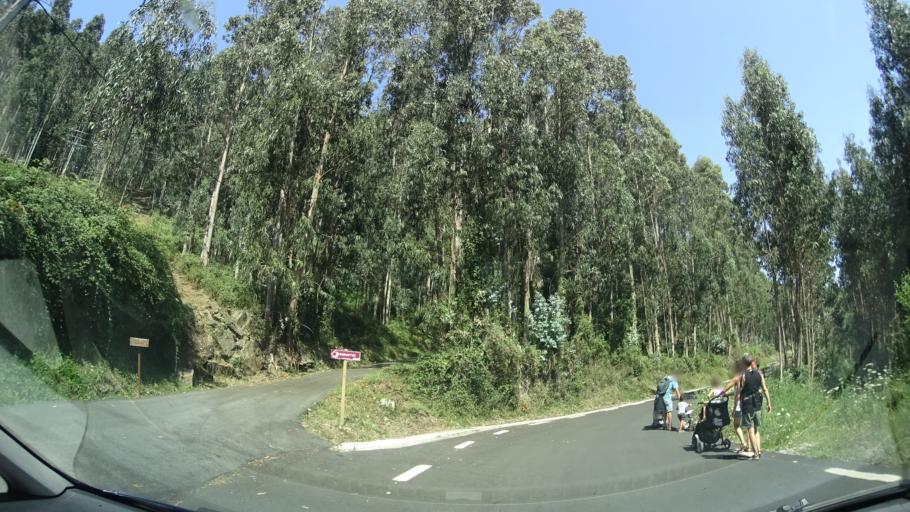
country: ES
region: Basque Country
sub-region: Bizkaia
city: Bermeo
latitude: 43.4470
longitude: -2.7511
